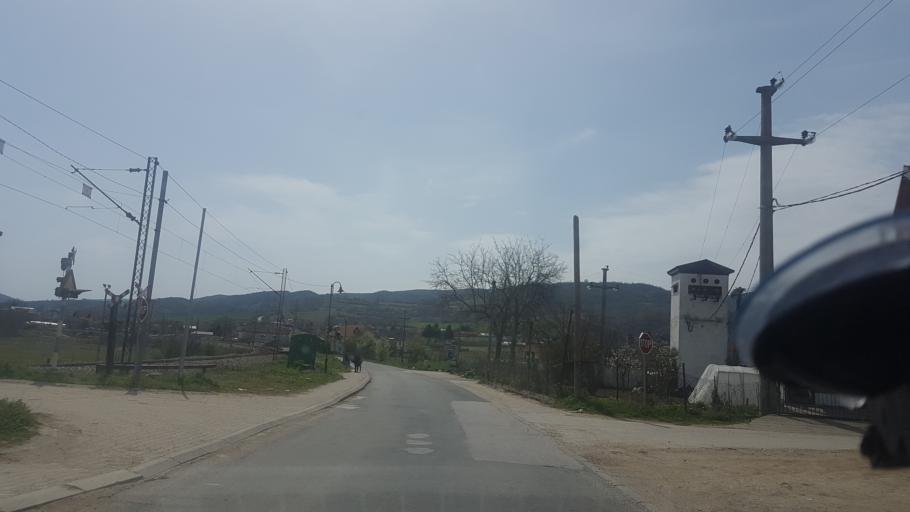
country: MK
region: Zelenikovo
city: Zelenikovo
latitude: 41.8866
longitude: 21.5877
